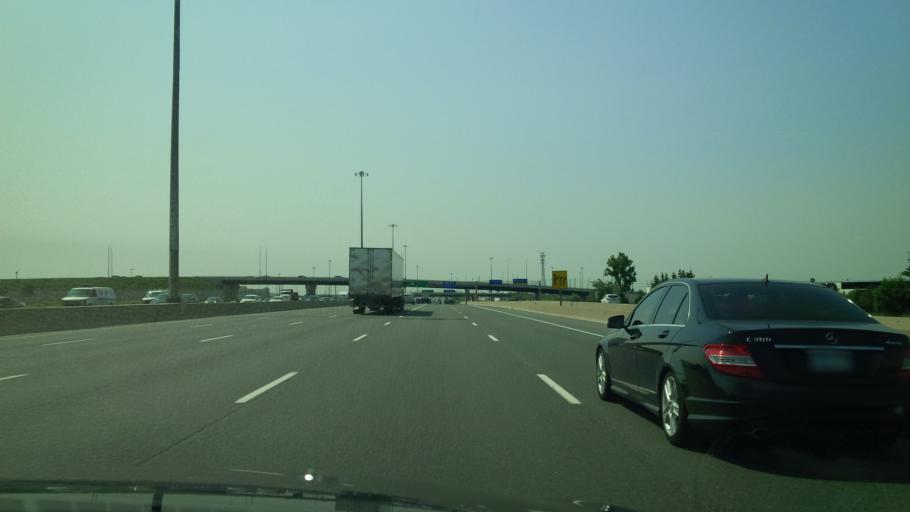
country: CA
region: Ontario
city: Vaughan
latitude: 43.7982
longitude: -79.5412
